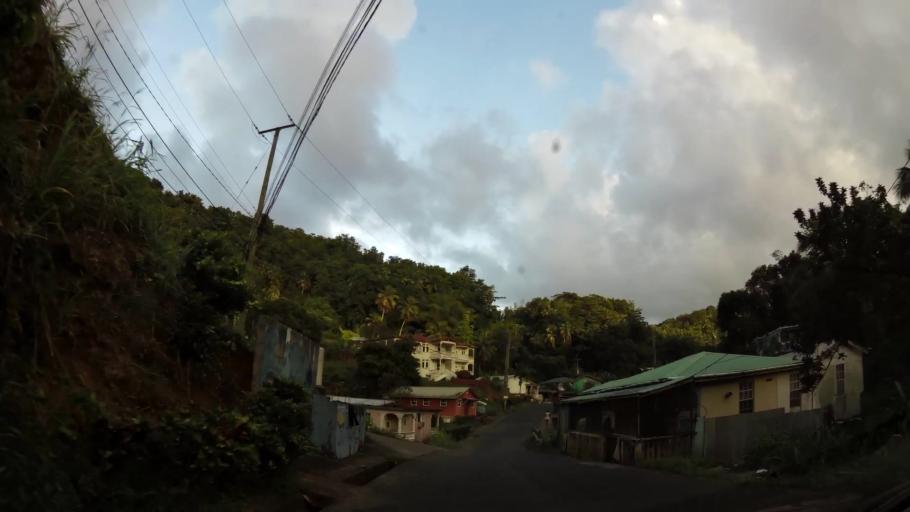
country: DM
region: Saint John
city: Portsmouth
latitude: 15.5853
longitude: -61.4128
